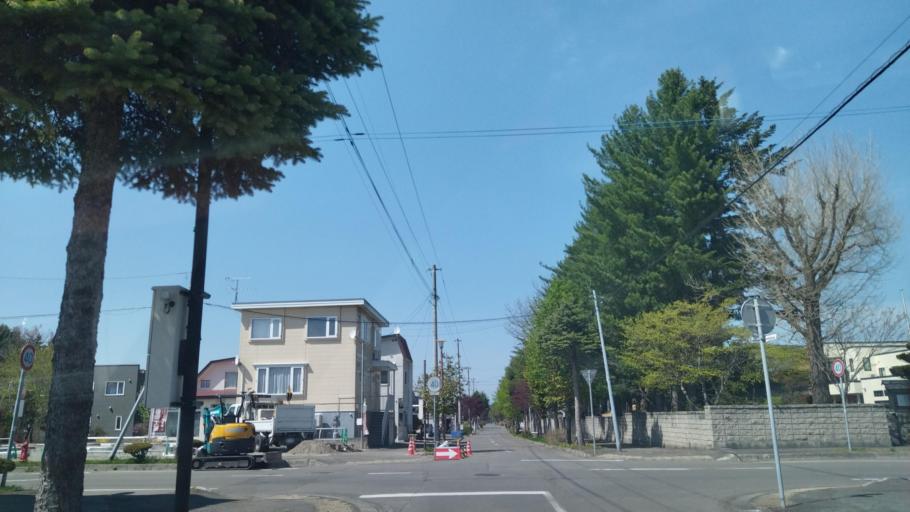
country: JP
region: Hokkaido
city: Obihiro
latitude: 42.9114
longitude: 143.0452
